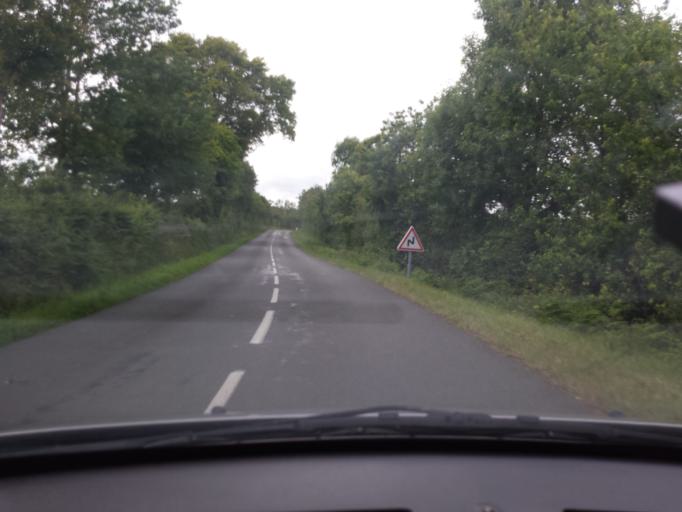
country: FR
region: Pays de la Loire
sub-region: Departement de la Vendee
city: Landeronde
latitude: 46.6617
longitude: -1.5823
